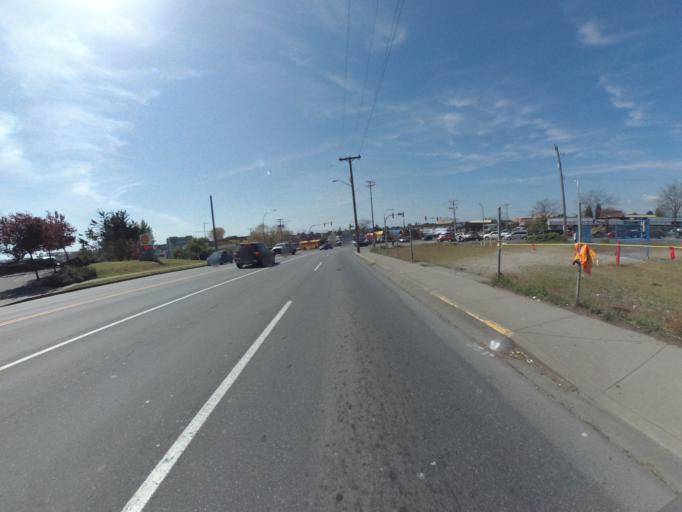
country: CA
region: British Columbia
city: Victoria
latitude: 48.4533
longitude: -123.3749
